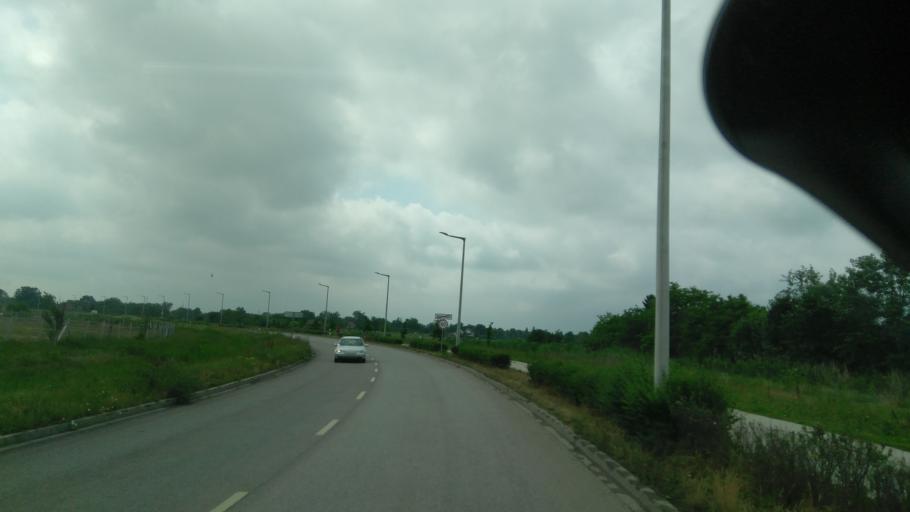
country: HU
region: Bekes
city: Bekescsaba
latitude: 46.6557
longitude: 21.0870
